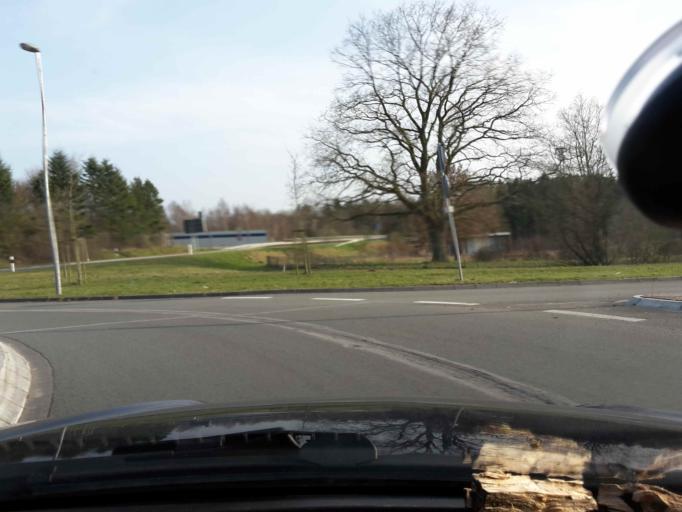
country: DE
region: Lower Saxony
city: Hollenstedt
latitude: 53.3600
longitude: 9.7102
